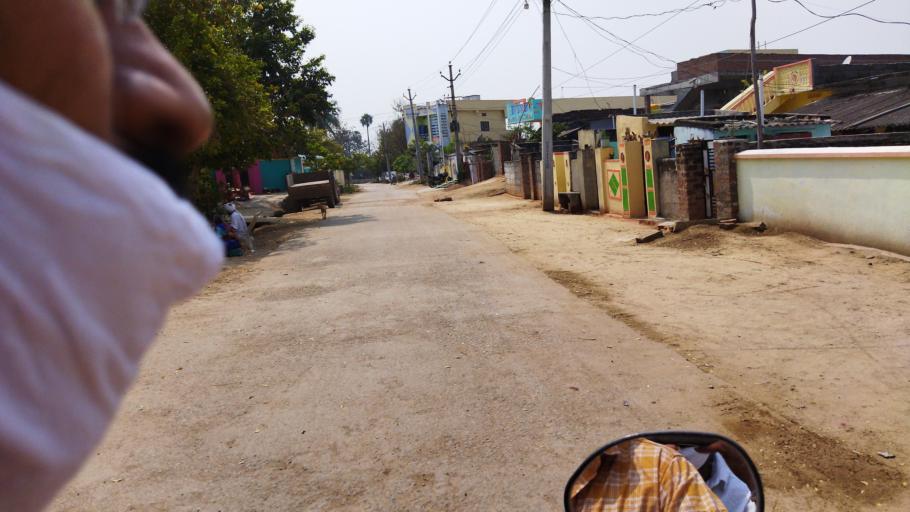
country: IN
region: Telangana
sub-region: Nalgonda
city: Nalgonda
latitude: 17.1619
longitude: 79.4234
